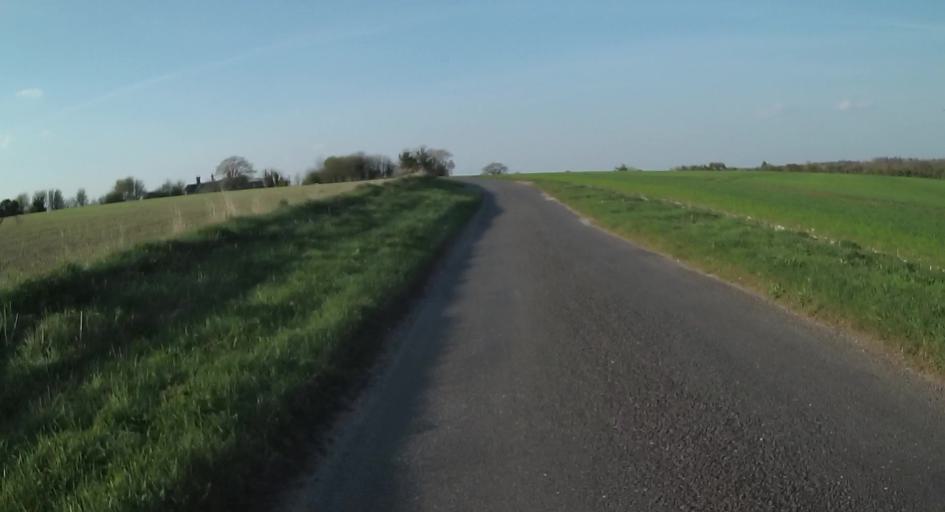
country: GB
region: England
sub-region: Hampshire
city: Basingstoke
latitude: 51.2288
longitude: -1.0919
